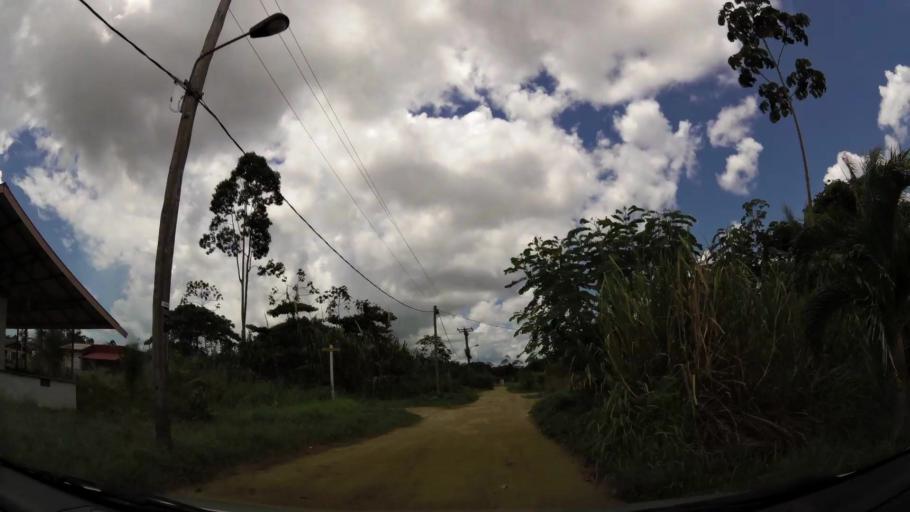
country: SR
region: Paramaribo
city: Paramaribo
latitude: 5.8587
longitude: -55.1557
